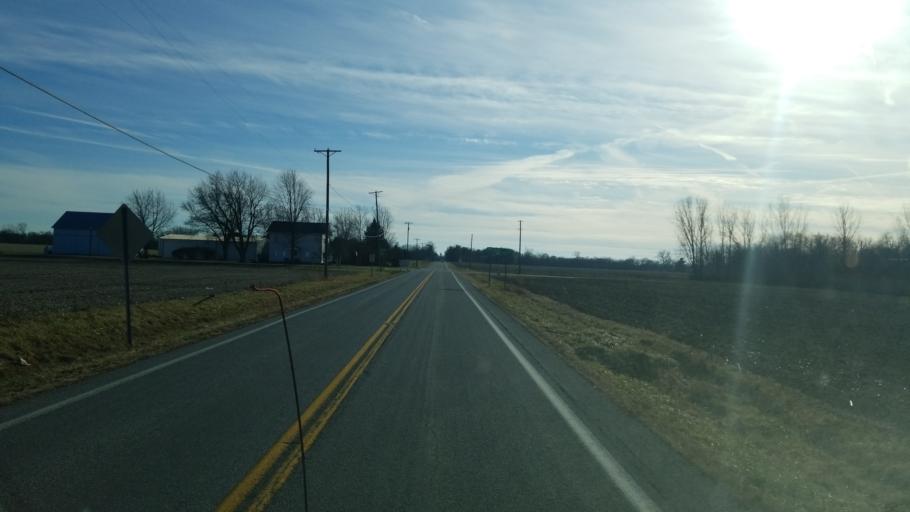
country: US
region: Ohio
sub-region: Sandusky County
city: Green Springs
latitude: 41.2897
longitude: -83.0523
